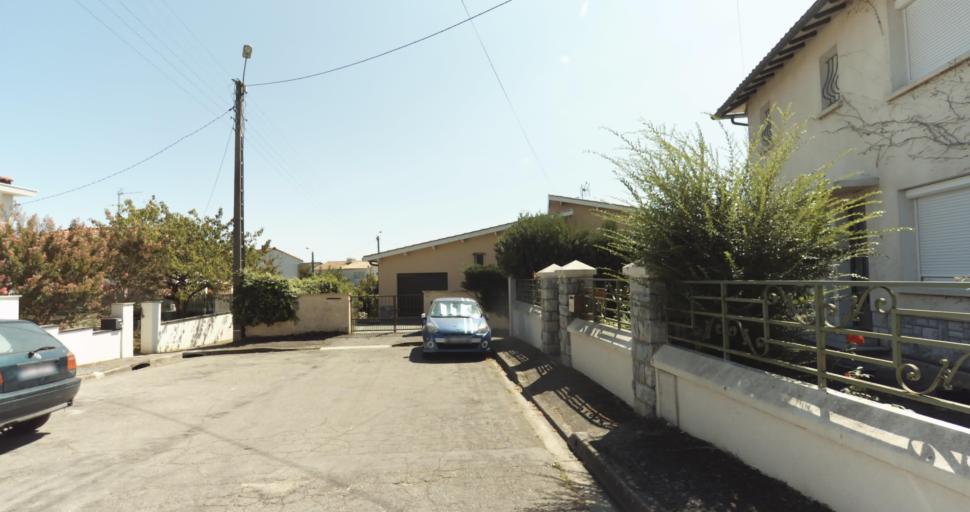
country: FR
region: Midi-Pyrenees
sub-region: Departement de la Haute-Garonne
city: L'Union
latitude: 43.6531
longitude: 1.4818
